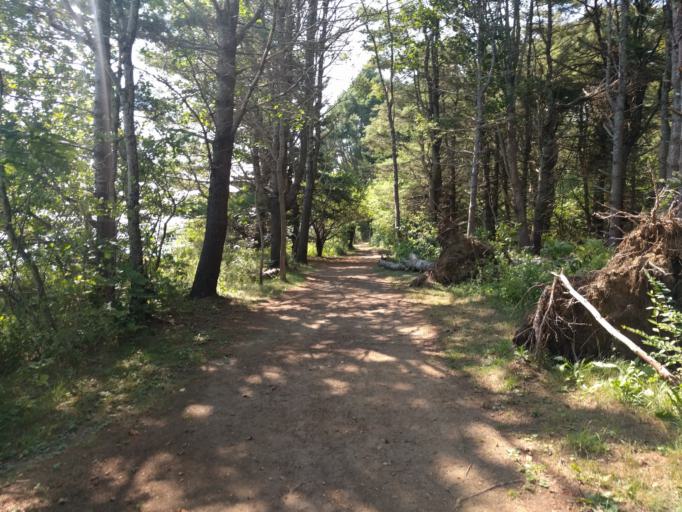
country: US
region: Maine
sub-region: Waldo County
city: Belfast
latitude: 44.4286
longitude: -68.9441
